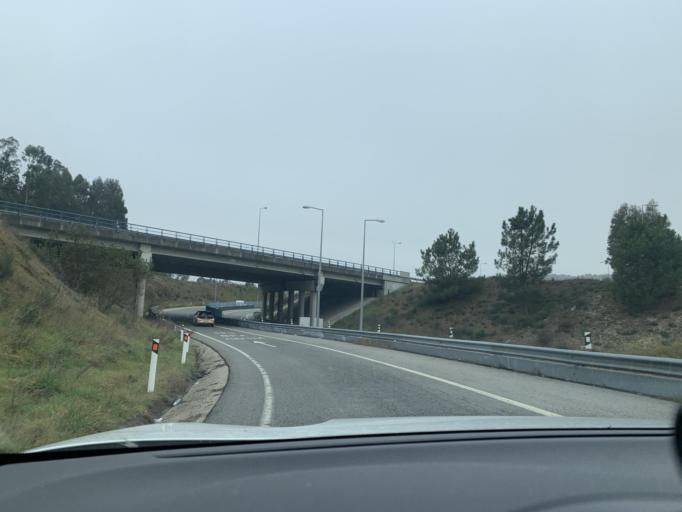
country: PT
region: Viseu
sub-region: Viseu
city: Viseu
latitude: 40.6259
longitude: -7.9592
